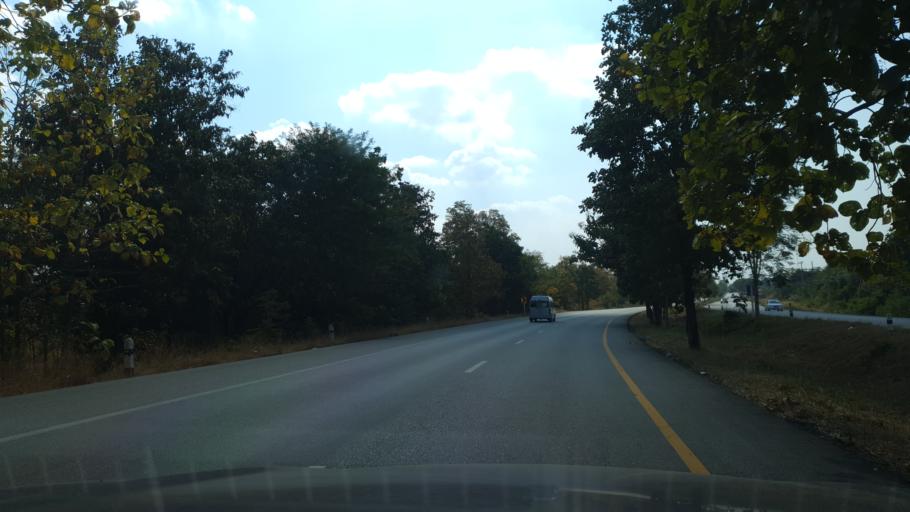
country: TH
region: Tak
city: Sam Ngao
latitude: 17.3037
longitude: 99.1475
